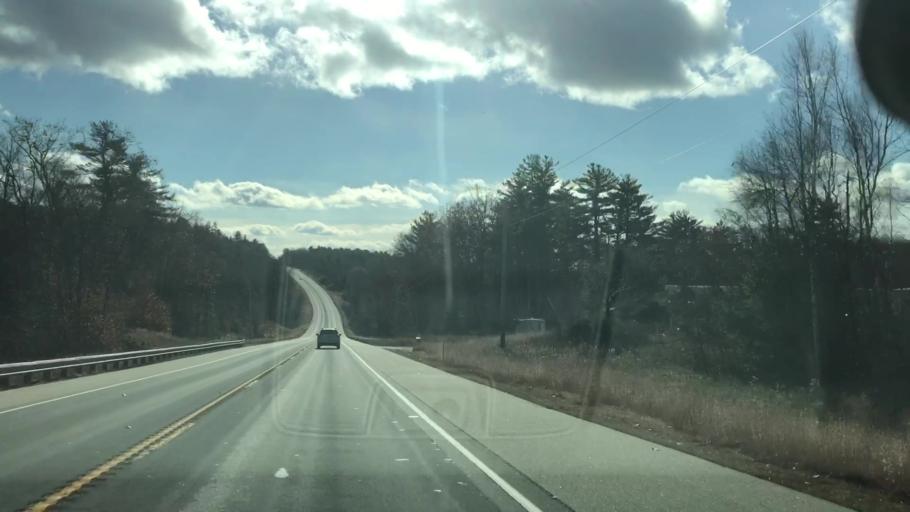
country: US
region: New Hampshire
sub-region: Strafford County
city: New Durham
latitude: 43.4818
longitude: -71.2277
